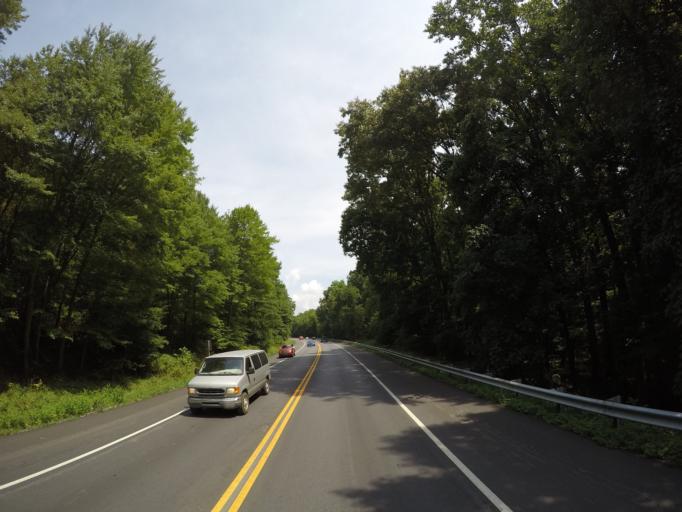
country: US
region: Maryland
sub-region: Prince George's County
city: Laurel
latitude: 39.1134
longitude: -76.8517
